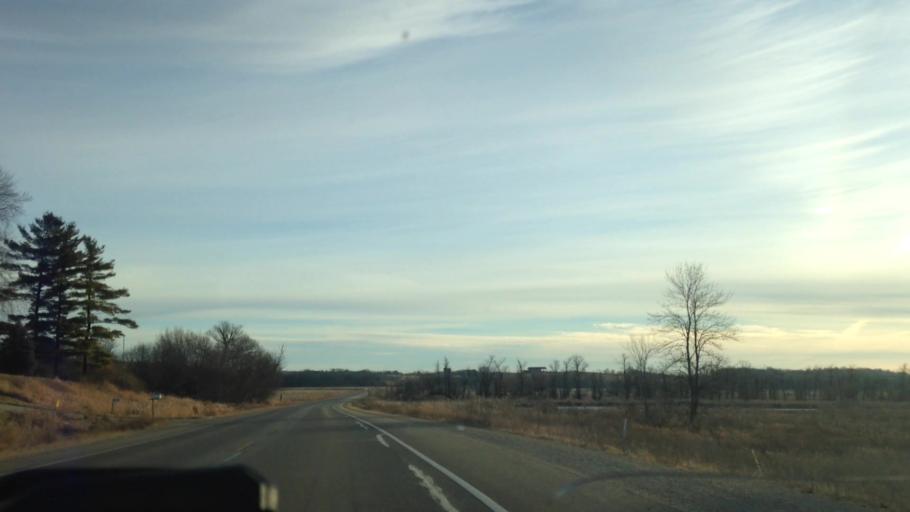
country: US
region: Wisconsin
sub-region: Dodge County
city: Theresa
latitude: 43.5365
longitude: -88.4263
